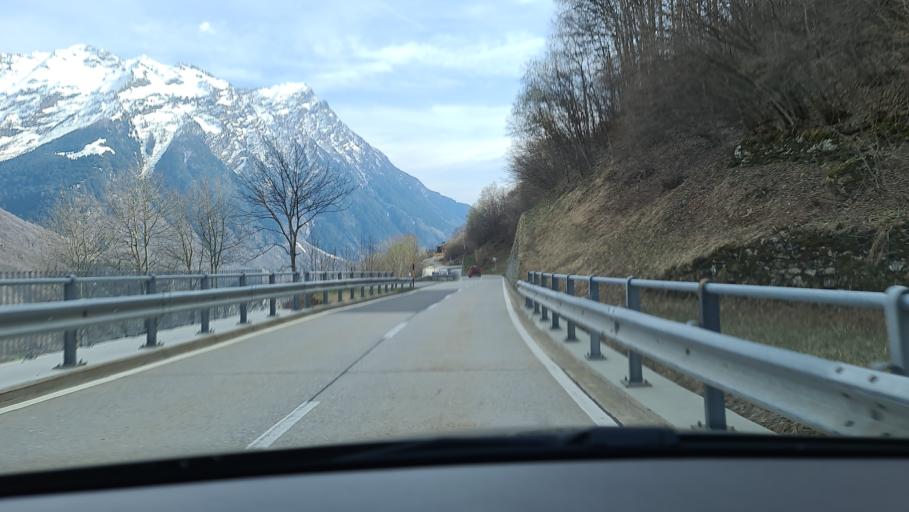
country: CH
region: Ticino
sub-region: Blenio District
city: Acquarossa
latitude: 46.5168
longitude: 8.9348
